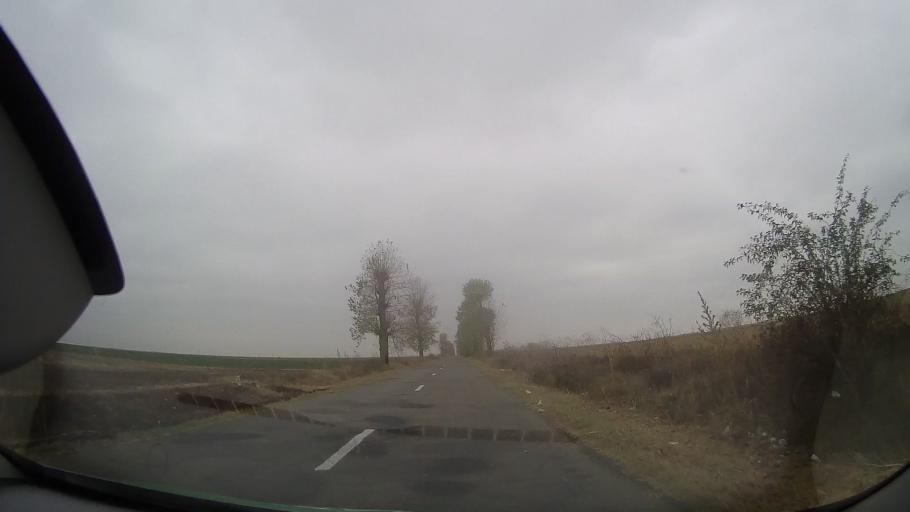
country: RO
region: Ialomita
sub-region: Comuna Grindu
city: Grindu
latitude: 44.7600
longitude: 26.8773
